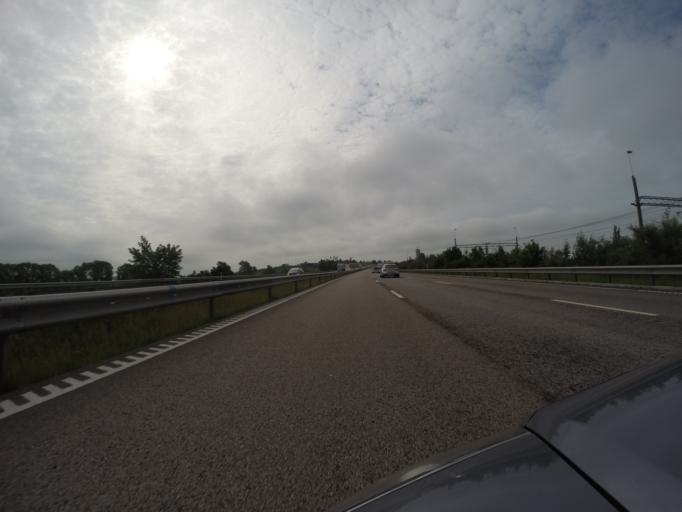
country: SE
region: Skane
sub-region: Helsingborg
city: Glumslov
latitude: 55.9445
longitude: 12.8142
